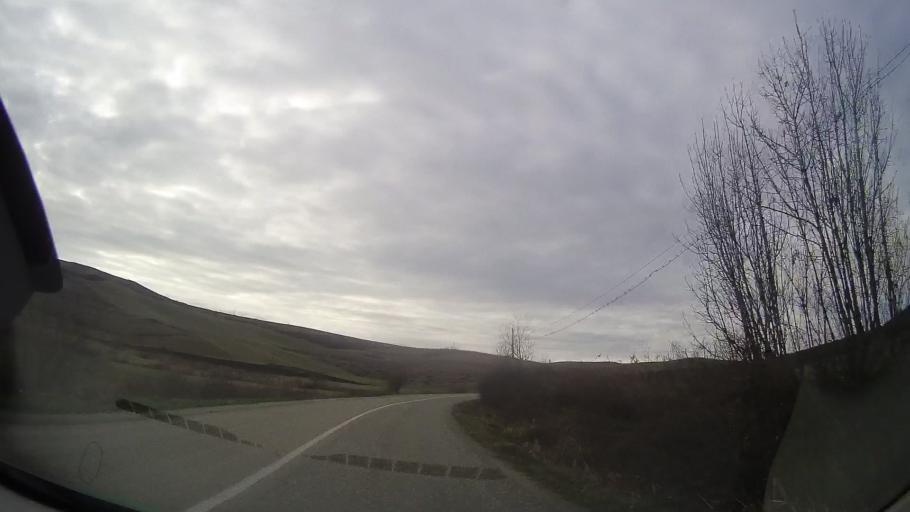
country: RO
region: Bistrita-Nasaud
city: Frunzi
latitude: 46.8937
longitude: 24.3050
